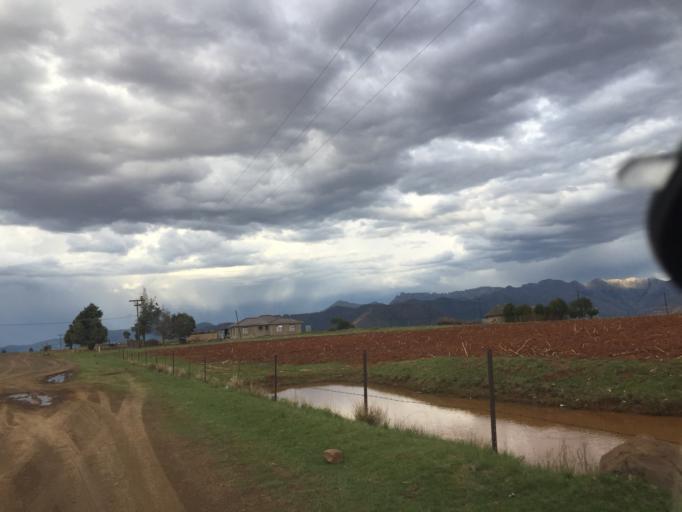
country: LS
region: Leribe
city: Leribe
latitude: -29.1534
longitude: 28.0391
